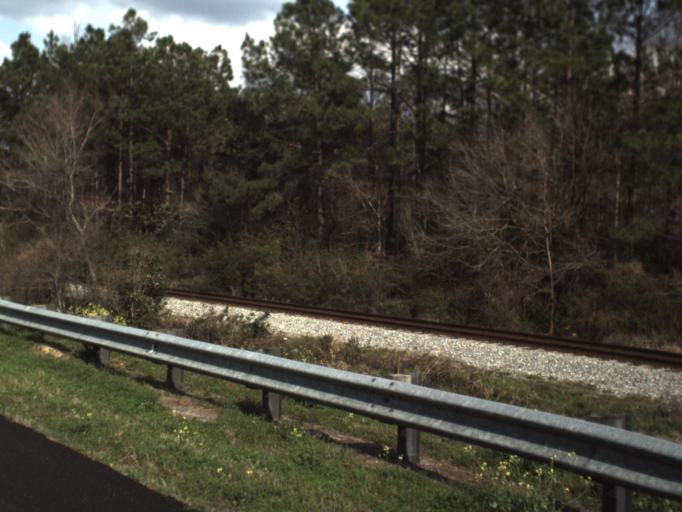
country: US
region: Florida
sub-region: Bay County
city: Youngstown
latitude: 30.3320
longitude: -85.4446
